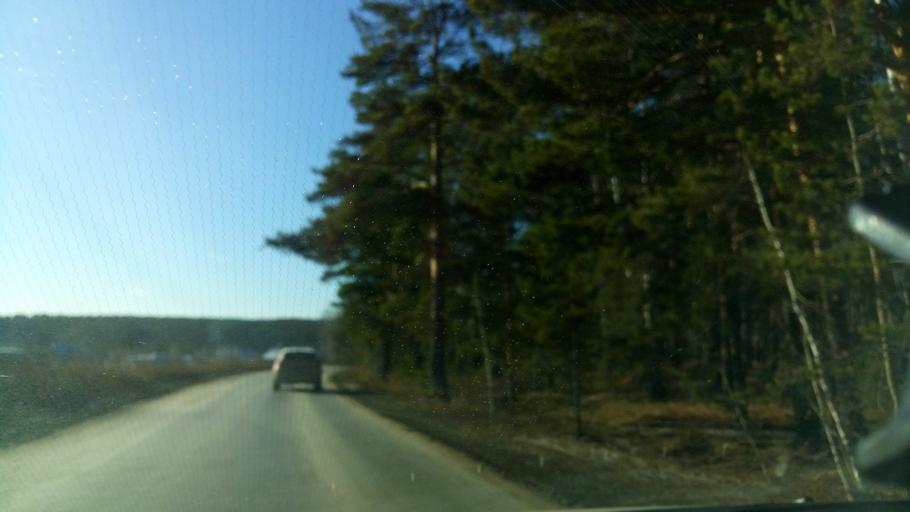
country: RU
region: Sverdlovsk
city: Gornyy Shchit
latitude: 56.7183
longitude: 60.5183
